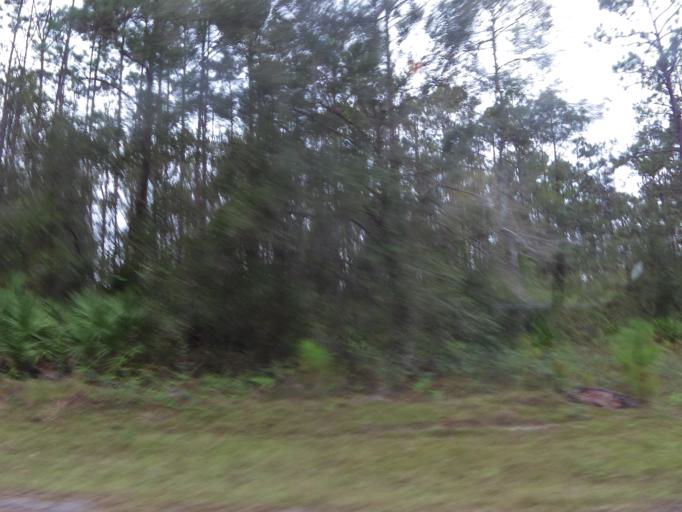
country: US
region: Florida
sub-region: Duval County
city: Baldwin
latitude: 30.2204
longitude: -81.8960
